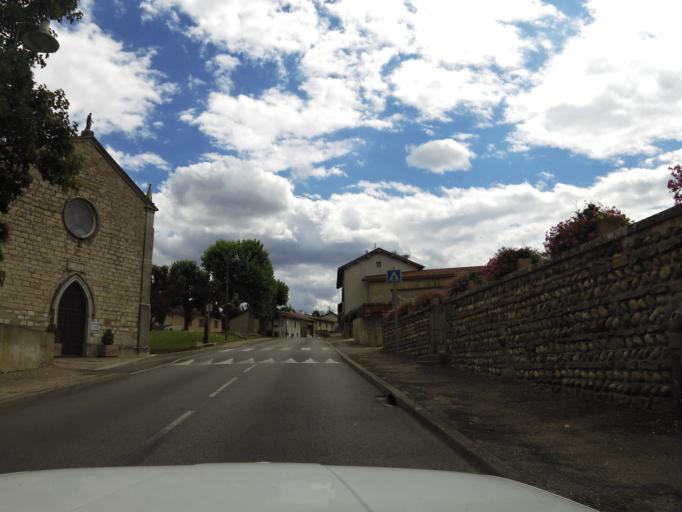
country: FR
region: Rhone-Alpes
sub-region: Departement de l'Ain
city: Saint-Jean-de-Niost
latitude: 45.8404
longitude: 5.2177
